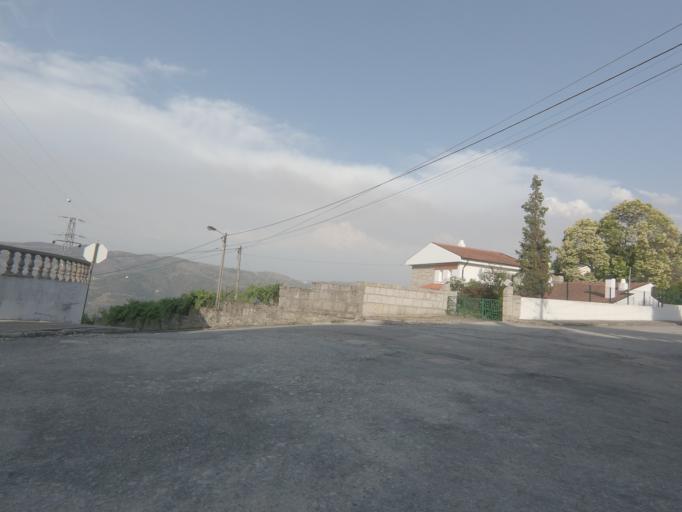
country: PT
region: Viseu
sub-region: Tabuaco
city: Tabuaco
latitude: 41.1139
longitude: -7.5641
